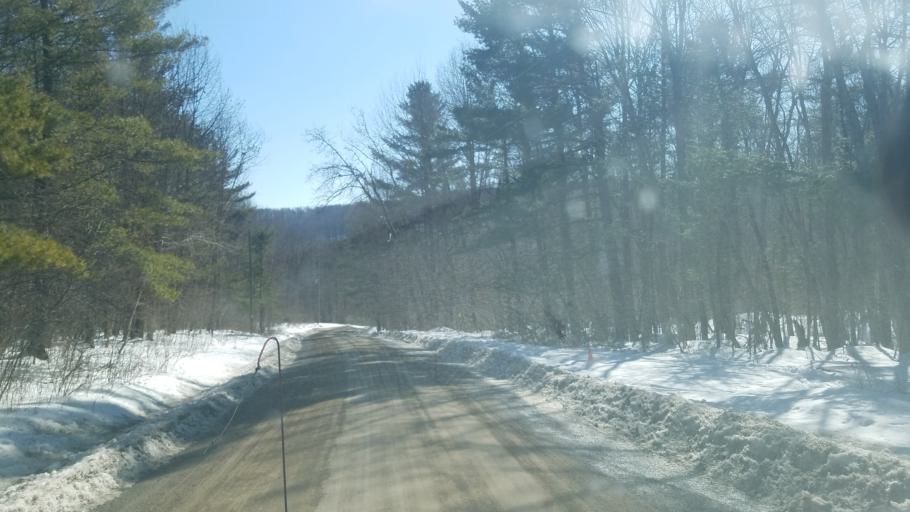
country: US
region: New York
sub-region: Allegany County
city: Alfred
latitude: 42.2497
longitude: -77.7272
